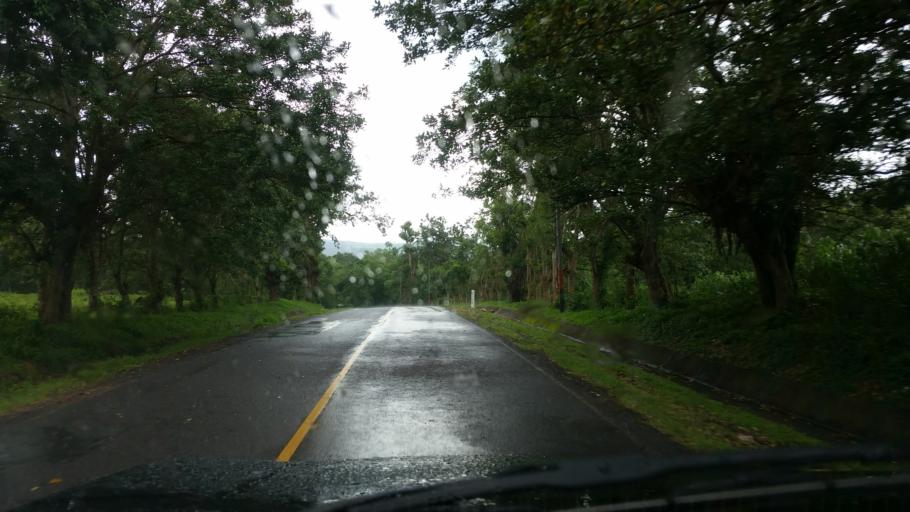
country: NI
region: Matagalpa
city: San Ramon
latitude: 13.0411
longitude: -85.7710
